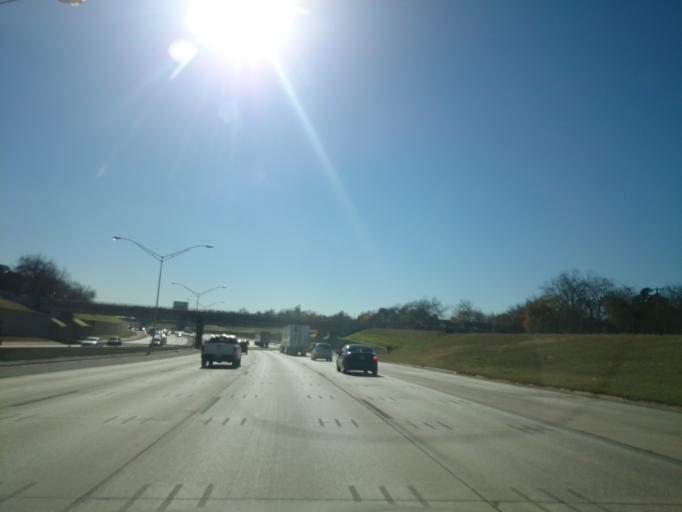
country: US
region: Oklahoma
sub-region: Oklahoma County
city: Warr Acres
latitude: 35.4905
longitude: -97.5797
